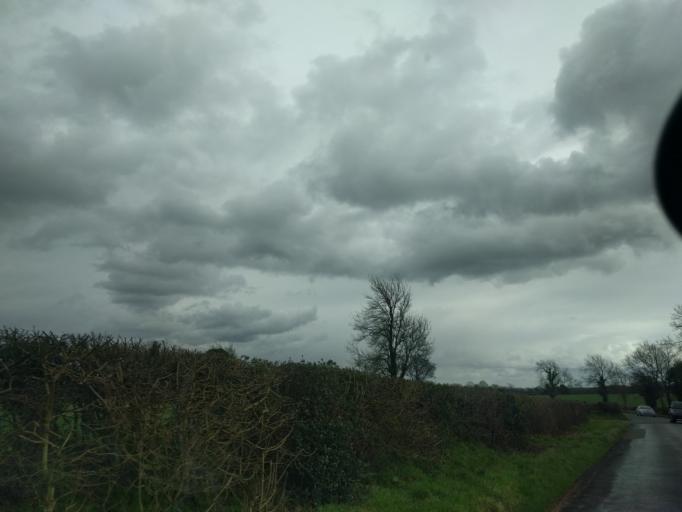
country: GB
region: England
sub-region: Gloucestershire
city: Nailsworth
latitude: 51.6379
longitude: -2.2407
